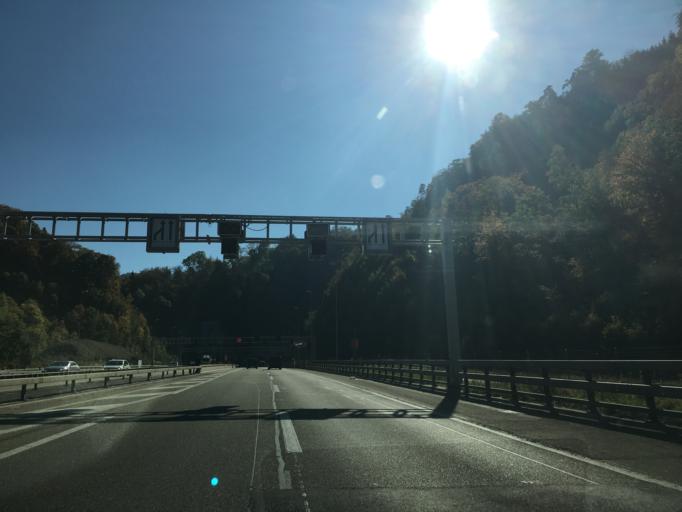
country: CH
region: Basel-Landschaft
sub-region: Bezirk Waldenburg
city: Diegten
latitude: 47.3824
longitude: 7.8166
